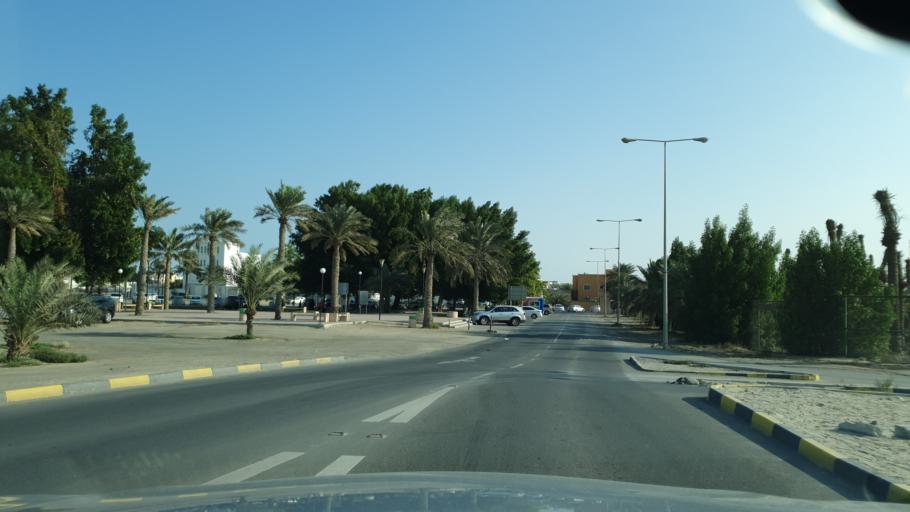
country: BH
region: Manama
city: Jidd Hafs
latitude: 26.2244
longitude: 50.4595
